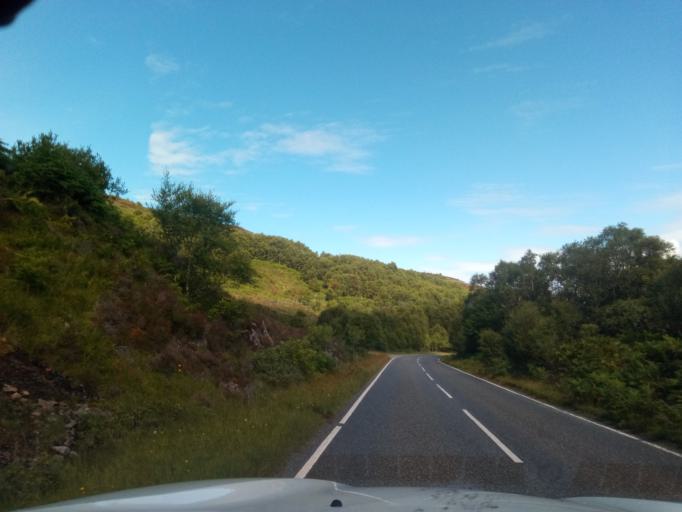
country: GB
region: Scotland
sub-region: Argyll and Bute
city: Isle Of Mull
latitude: 56.8162
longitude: -5.8211
